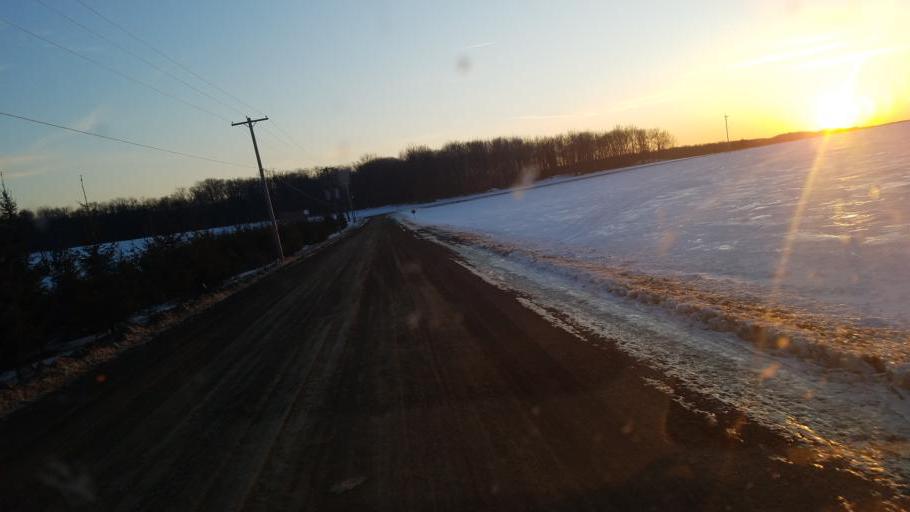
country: US
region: Pennsylvania
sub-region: Tioga County
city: Westfield
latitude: 42.0027
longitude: -77.6888
